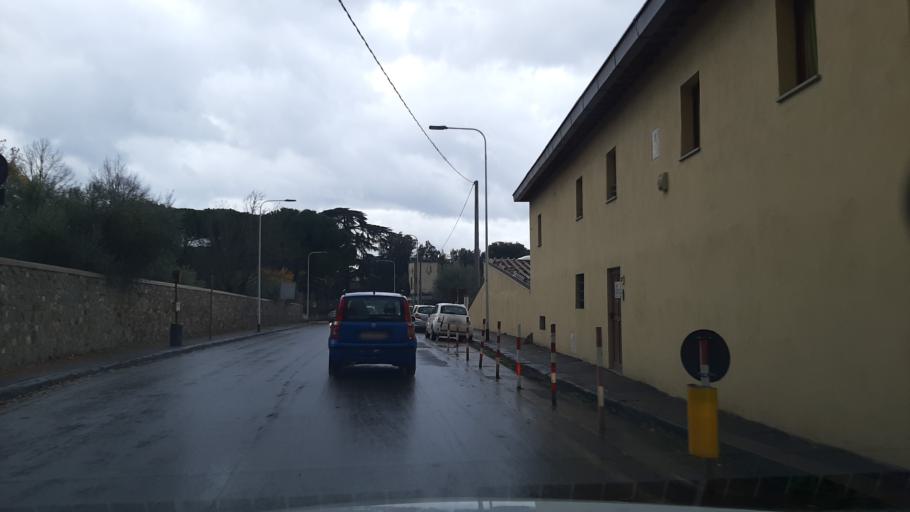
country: IT
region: Tuscany
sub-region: Province of Florence
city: Florence
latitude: 43.8114
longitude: 11.2500
